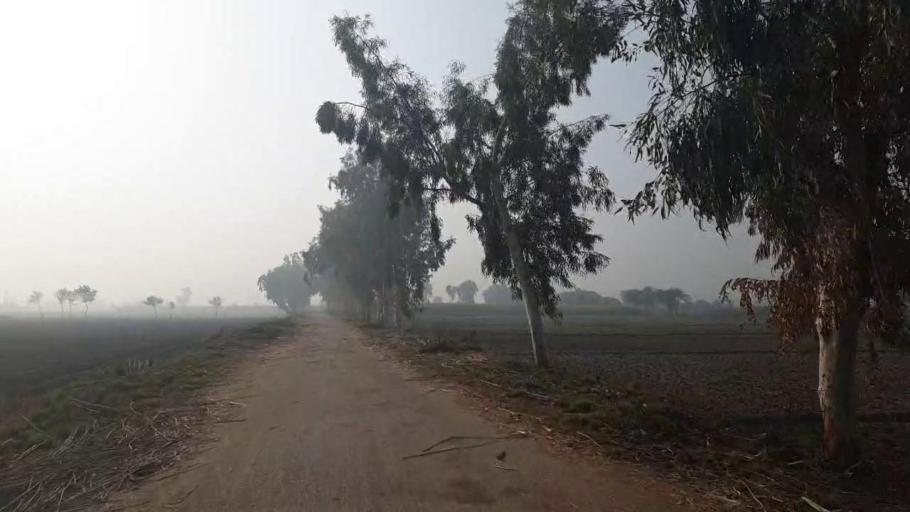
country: PK
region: Sindh
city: Tando Adam
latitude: 25.8041
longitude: 68.6173
